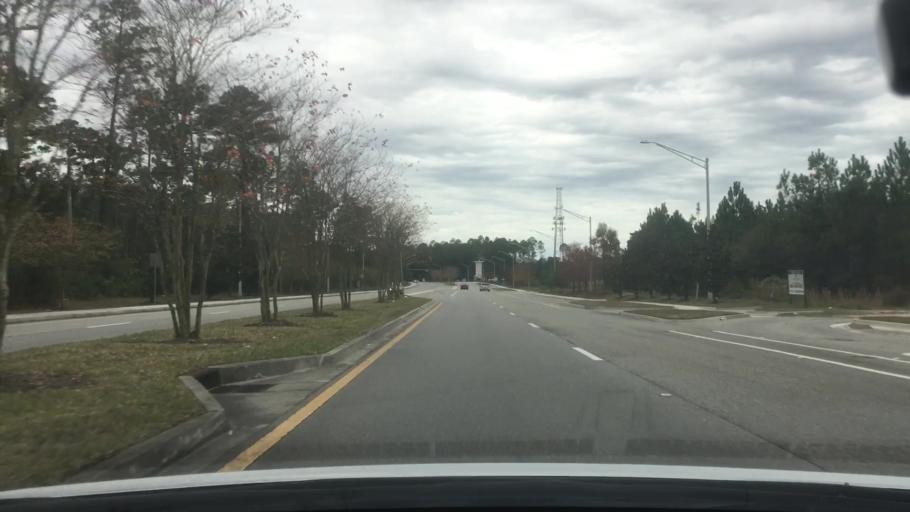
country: US
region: Florida
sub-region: Nassau County
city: Yulee
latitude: 30.4910
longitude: -81.6276
